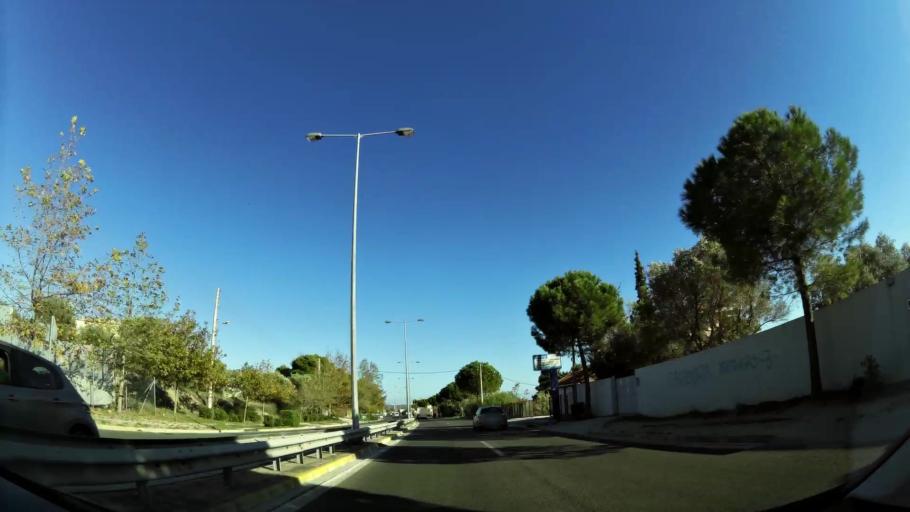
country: GR
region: Attica
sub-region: Nomarchia Anatolikis Attikis
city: Pikermi
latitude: 37.9980
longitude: 23.9206
